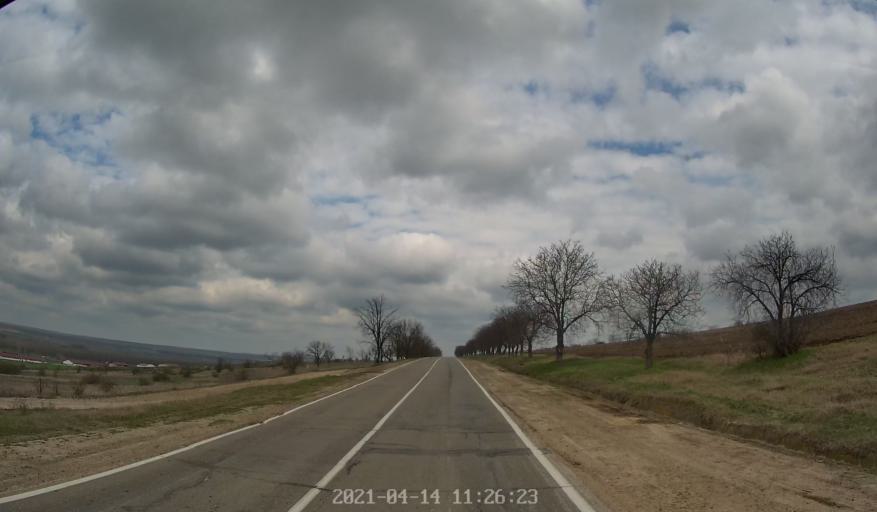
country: MD
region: Criuleni
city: Criuleni
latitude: 47.1634
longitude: 29.1635
